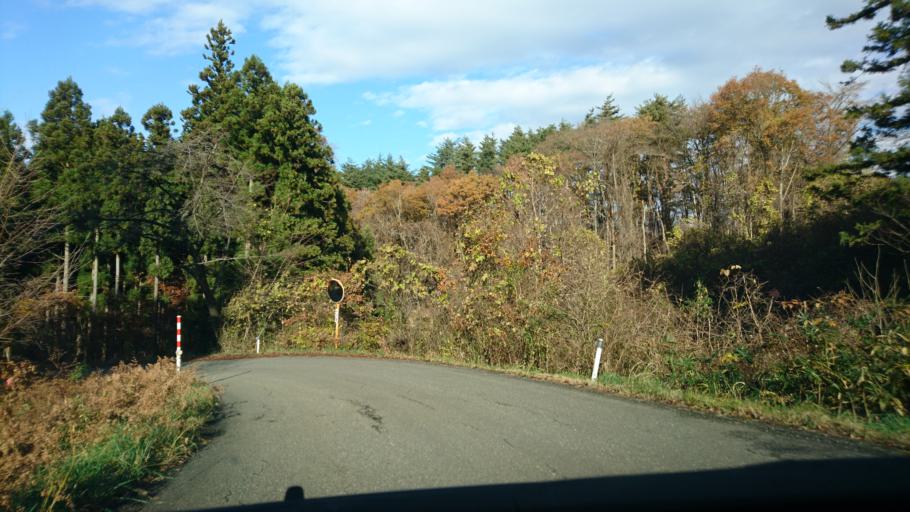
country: JP
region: Iwate
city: Mizusawa
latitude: 39.0254
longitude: 141.1691
